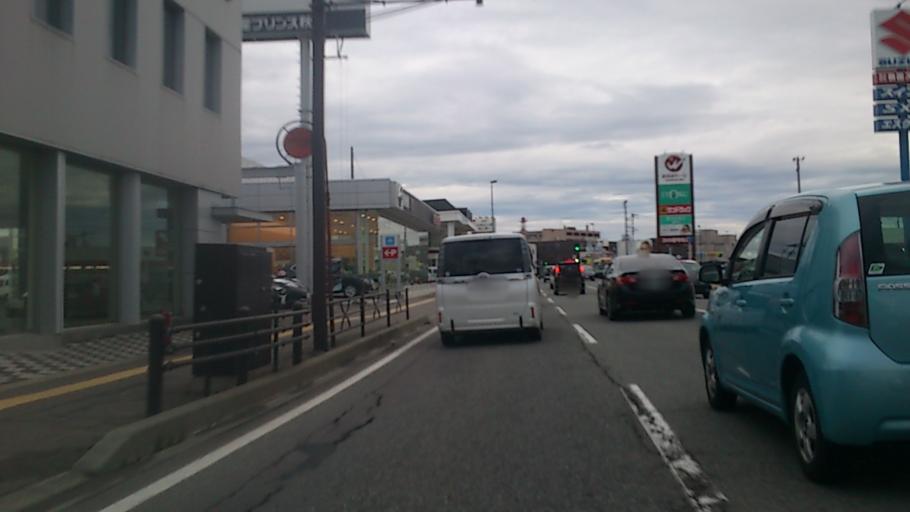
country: JP
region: Akita
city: Akita Shi
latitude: 39.7267
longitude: 140.1066
